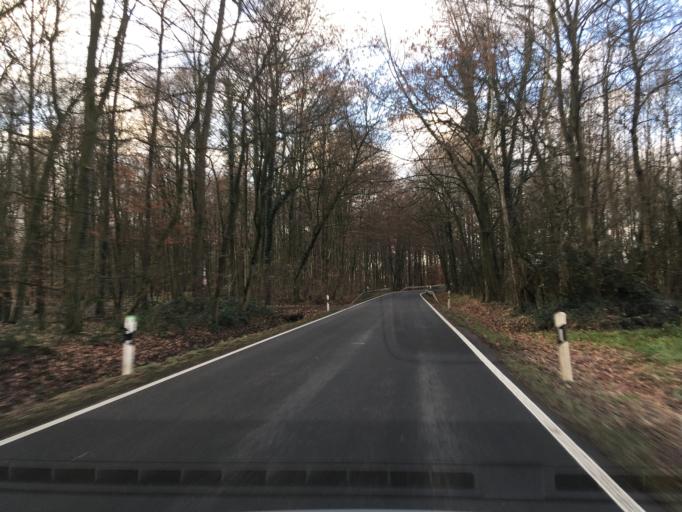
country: DE
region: North Rhine-Westphalia
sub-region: Regierungsbezirk Munster
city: Gescher
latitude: 51.9577
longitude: 7.0286
